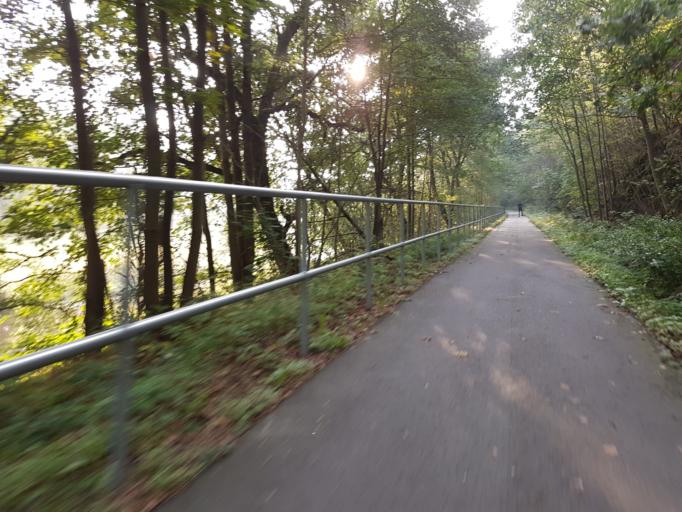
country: DE
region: Saxony
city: Claussnitz
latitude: 50.9157
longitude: 12.8835
